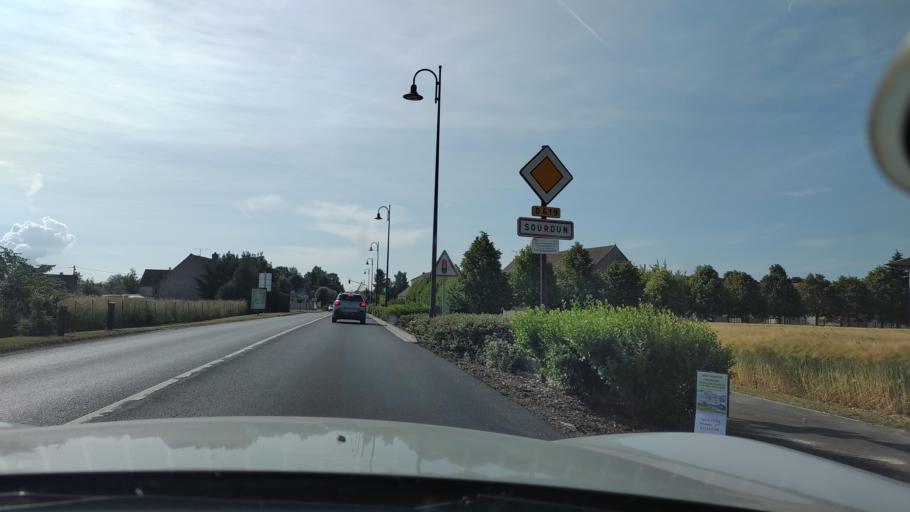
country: FR
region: Ile-de-France
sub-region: Departement de Seine-et-Marne
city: Sourdun
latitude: 48.5405
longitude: 3.3476
